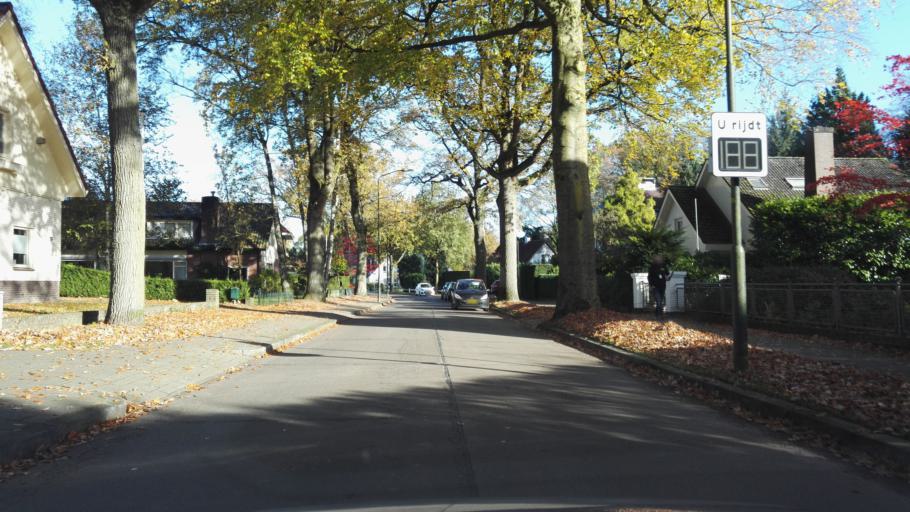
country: NL
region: Gelderland
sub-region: Gemeente Apeldoorn
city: Apeldoorn
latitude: 52.2257
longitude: 5.9671
